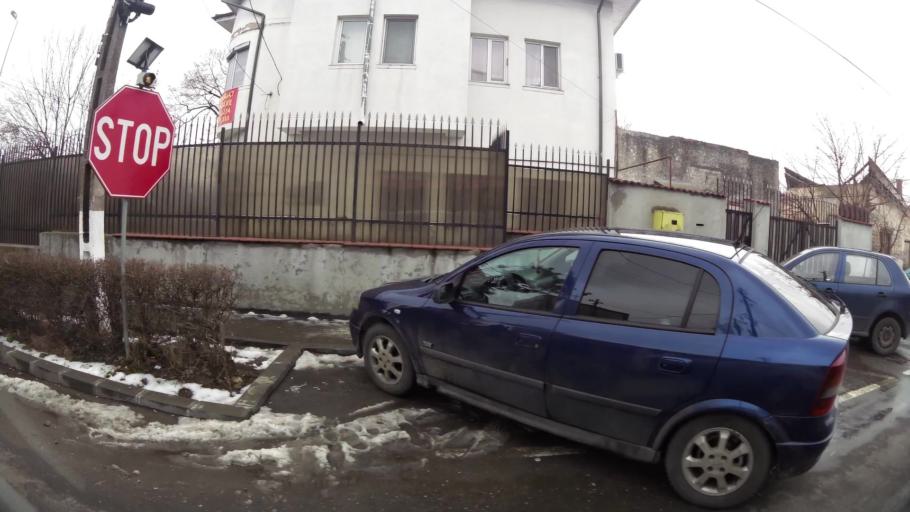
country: RO
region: Ilfov
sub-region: Comuna Afumati
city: Afumati
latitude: 44.5238
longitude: 26.2495
